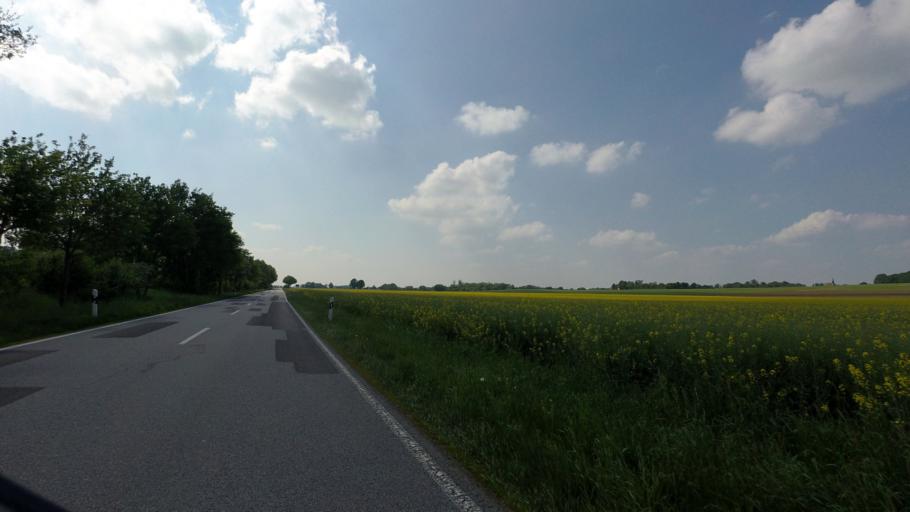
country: DE
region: Saxony
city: Weissenberg
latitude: 51.1862
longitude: 14.6674
